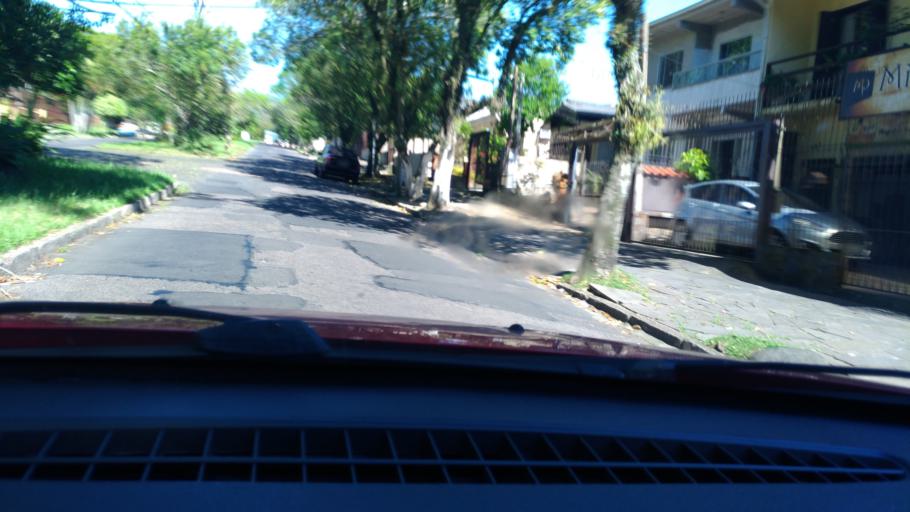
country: BR
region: Rio Grande do Sul
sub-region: Cachoeirinha
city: Cachoeirinha
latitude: -30.0332
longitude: -51.1308
